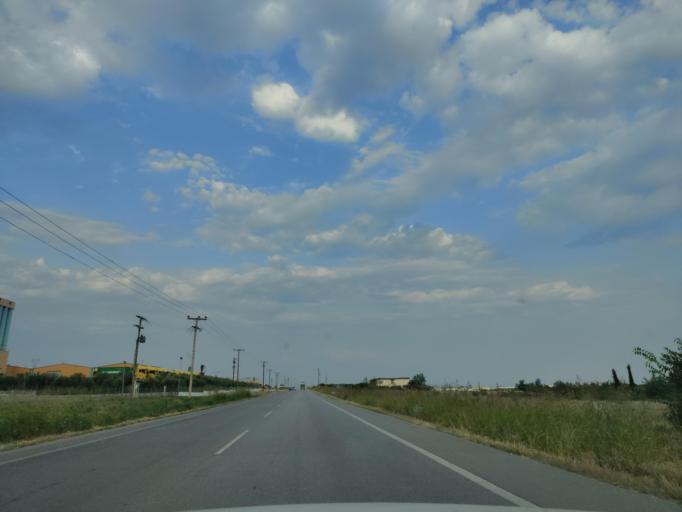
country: GR
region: East Macedonia and Thrace
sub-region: Nomos Dramas
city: Prosotsani
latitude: 41.1795
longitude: 23.9908
